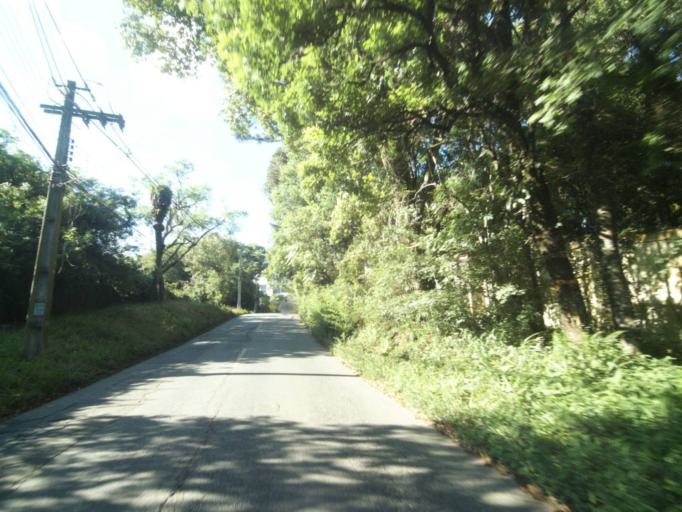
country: BR
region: Parana
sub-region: Curitiba
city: Curitiba
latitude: -25.4430
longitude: -49.3225
